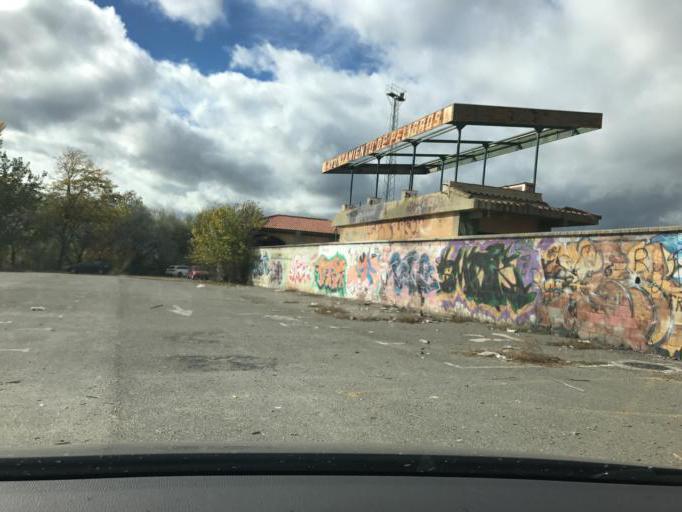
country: ES
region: Andalusia
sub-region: Provincia de Granada
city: Peligros
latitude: 37.2337
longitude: -3.6347
